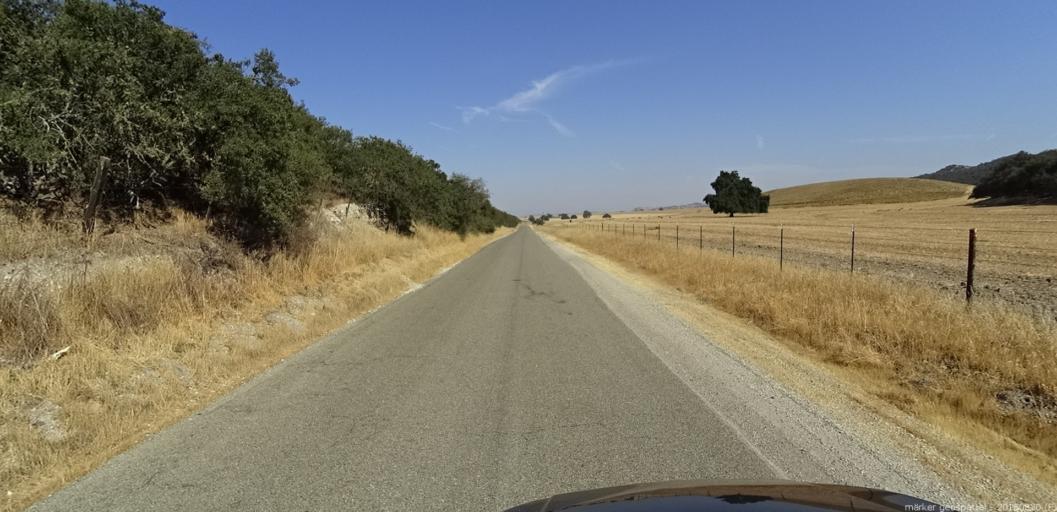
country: US
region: California
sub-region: Monterey County
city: King City
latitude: 36.1143
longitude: -121.1116
